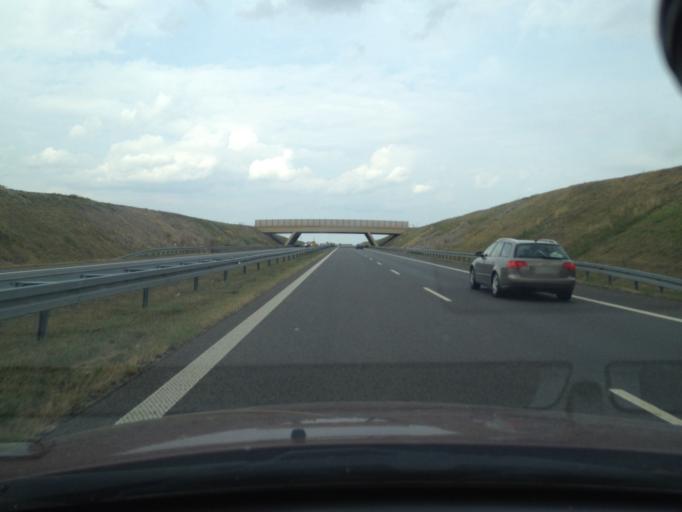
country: PL
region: West Pomeranian Voivodeship
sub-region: Powiat pyrzycki
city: Kozielice
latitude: 53.0648
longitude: 14.8626
